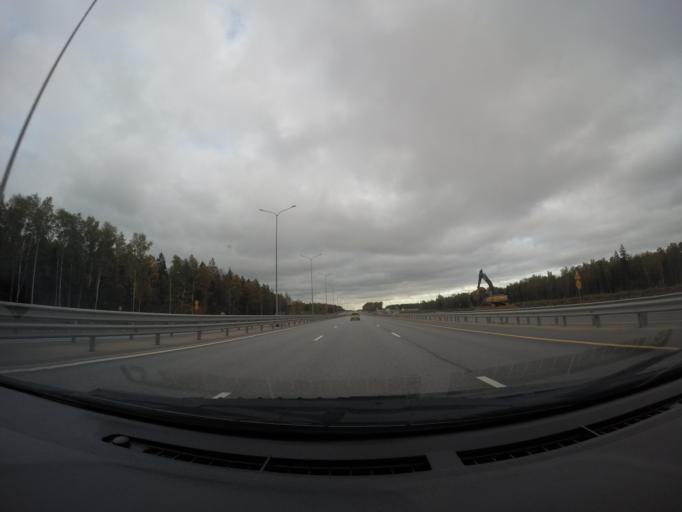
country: RU
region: Moskovskaya
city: Kubinka
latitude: 55.5807
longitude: 36.7943
